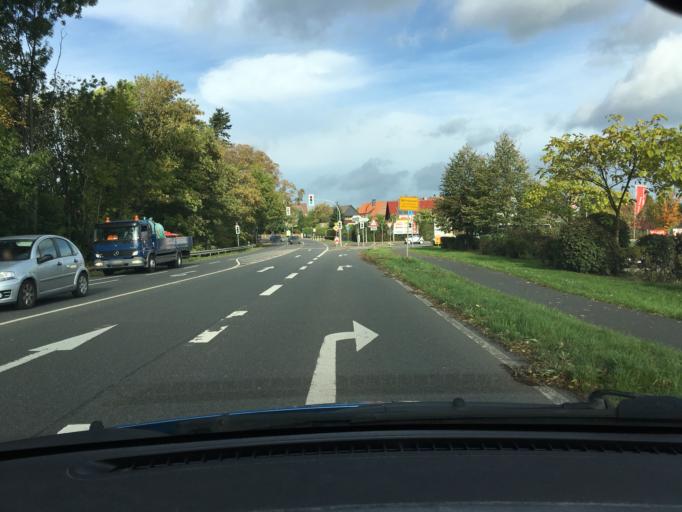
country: DE
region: Lower Saxony
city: Bad Nenndorf
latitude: 52.3338
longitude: 9.4010
